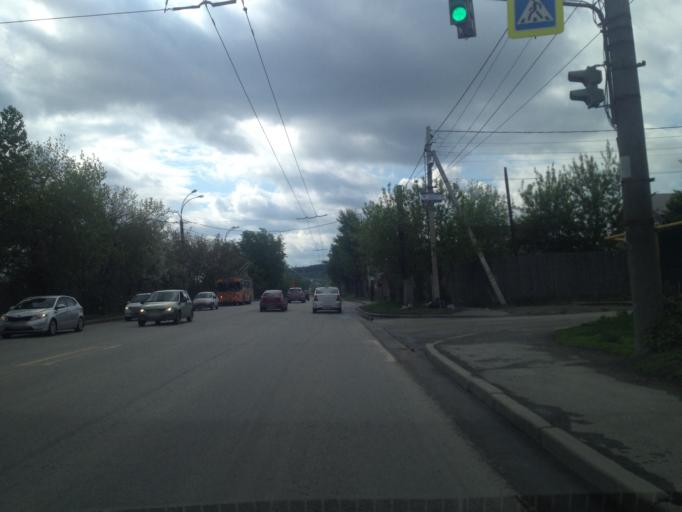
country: RU
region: Sverdlovsk
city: Istok
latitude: 56.7538
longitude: 60.6758
